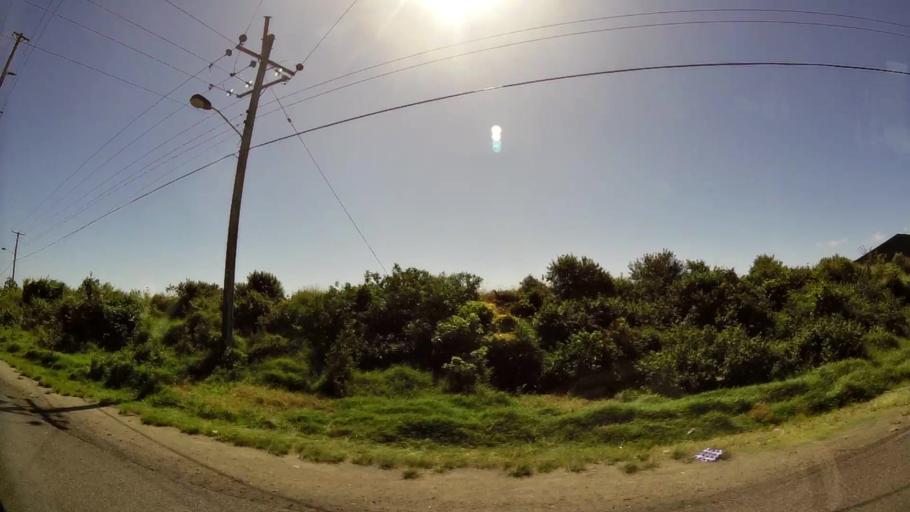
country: LC
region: Vieux-Fort
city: Vieux Fort
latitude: 13.7525
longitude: -60.9458
